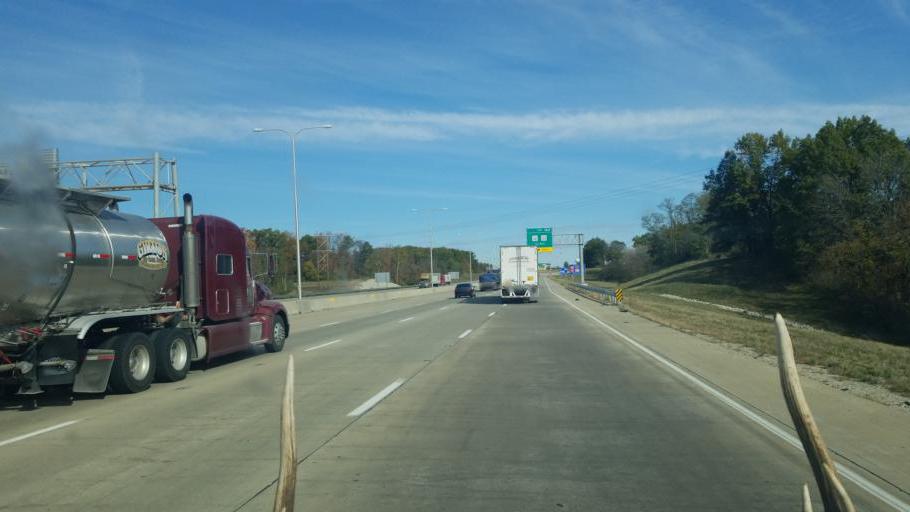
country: US
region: Illinois
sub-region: Effingham County
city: Effingham
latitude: 39.1242
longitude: -88.5672
